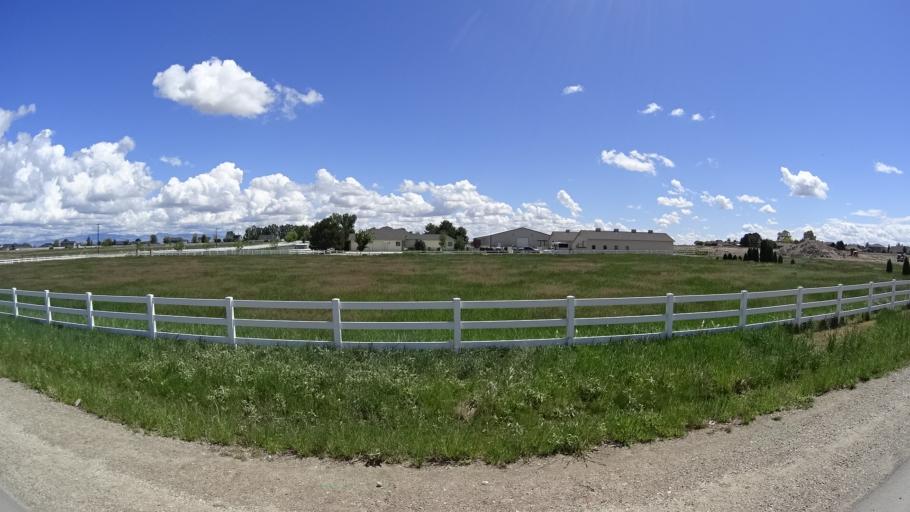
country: US
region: Idaho
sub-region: Ada County
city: Kuna
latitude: 43.5165
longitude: -116.4337
